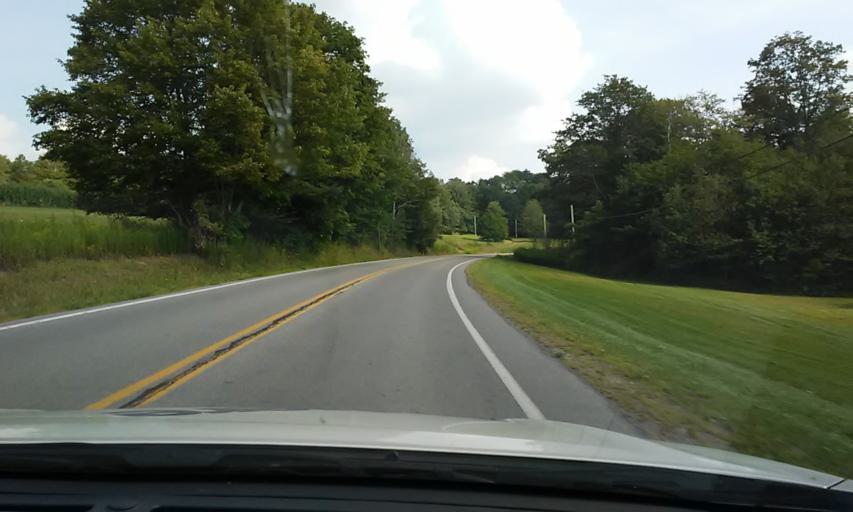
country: US
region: Pennsylvania
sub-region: Potter County
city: Coudersport
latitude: 41.8623
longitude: -77.8288
